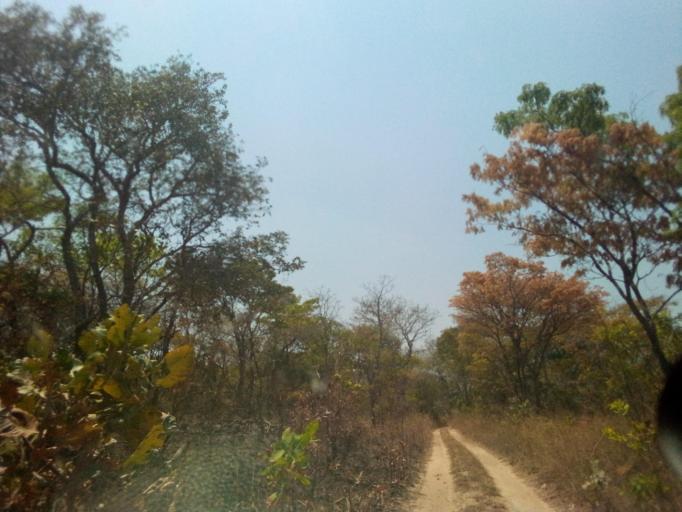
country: ZM
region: Copperbelt
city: Kataba
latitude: -12.2504
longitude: 30.3915
